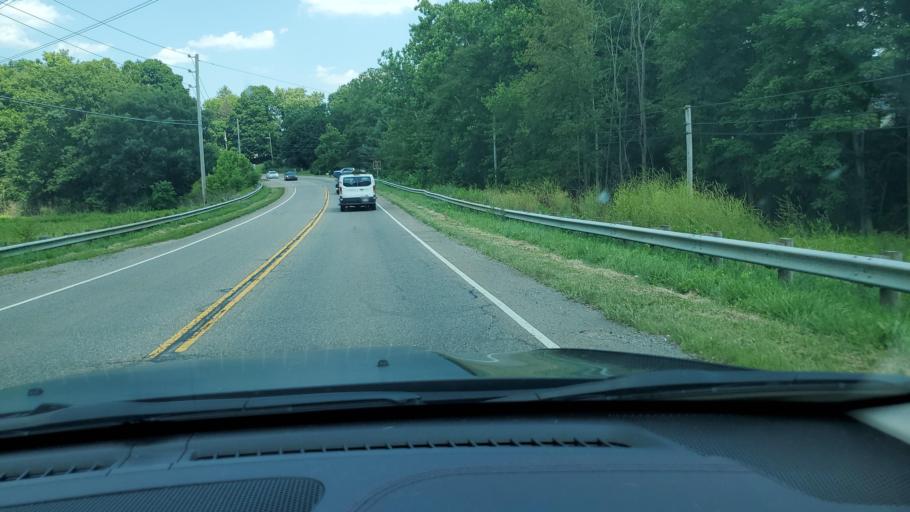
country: US
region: Ohio
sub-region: Trumbull County
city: McKinley Heights
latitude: 41.1825
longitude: -80.7063
